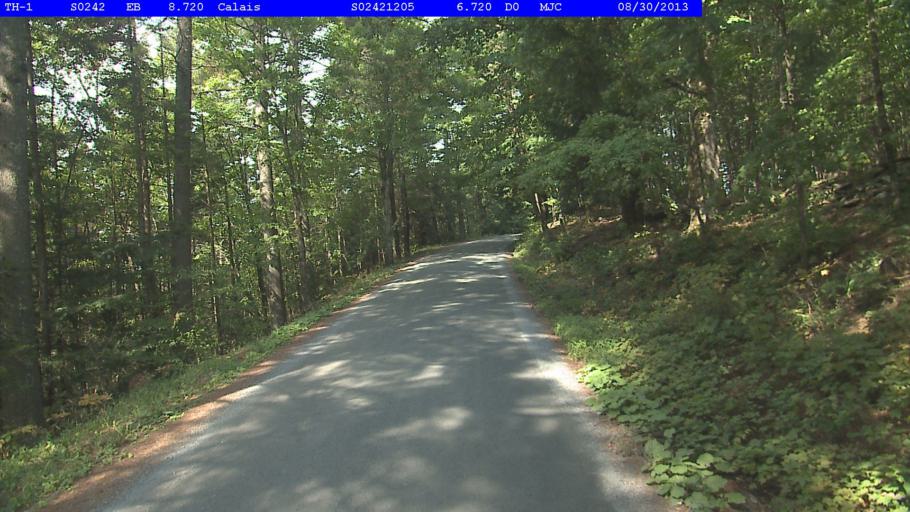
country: US
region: Vermont
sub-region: Caledonia County
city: Hardwick
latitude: 44.3961
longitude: -72.4386
